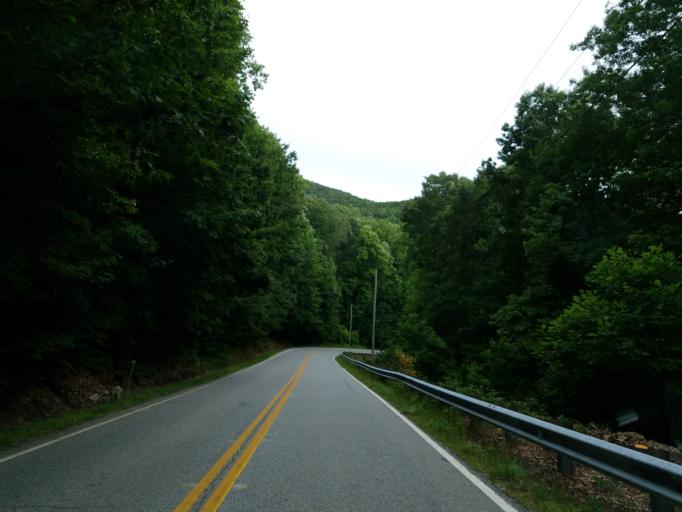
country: US
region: Georgia
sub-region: Lumpkin County
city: Dahlonega
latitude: 34.6838
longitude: -84.0092
